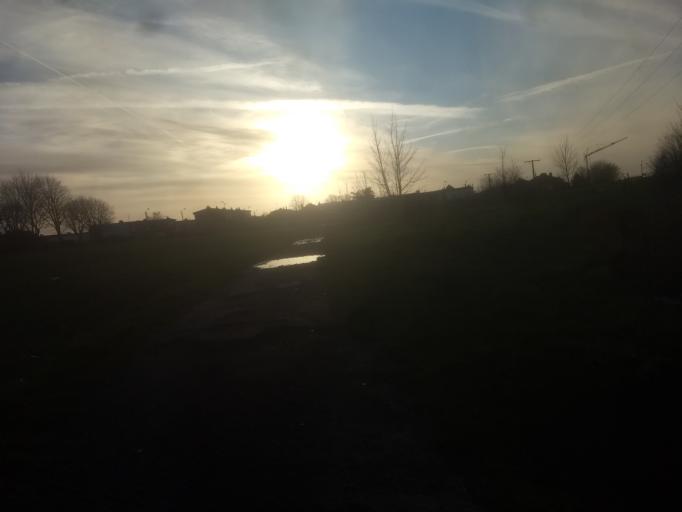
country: FR
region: Nord-Pas-de-Calais
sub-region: Departement du Pas-de-Calais
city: Beaurains
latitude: 50.2739
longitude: 2.7914
